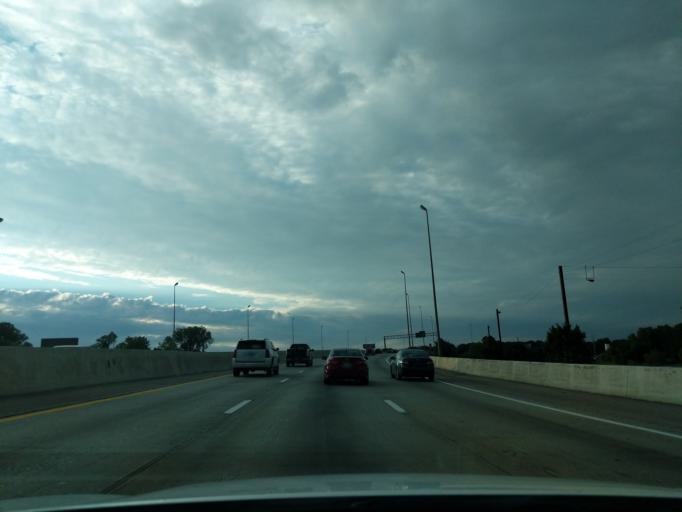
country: US
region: Tennessee
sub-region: Shelby County
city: New South Memphis
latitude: 35.0813
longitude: -90.0728
